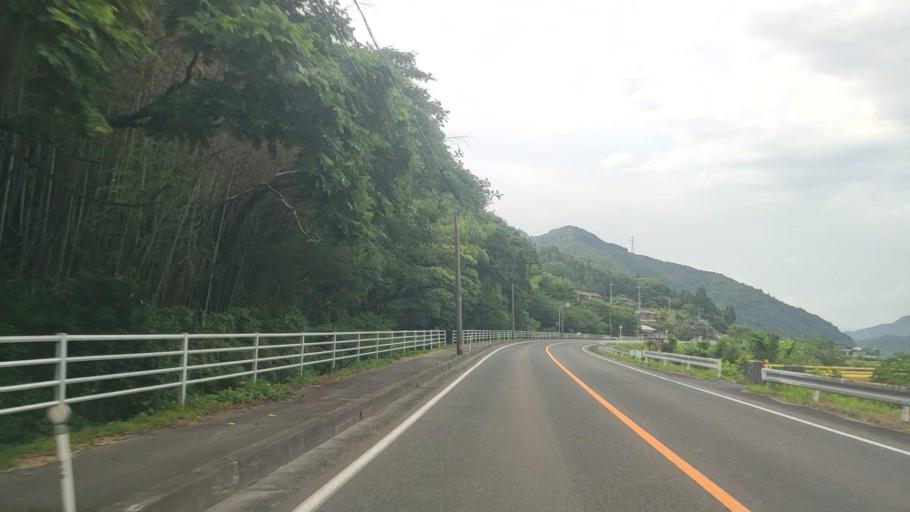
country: JP
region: Tottori
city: Kurayoshi
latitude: 35.3441
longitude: 133.8410
